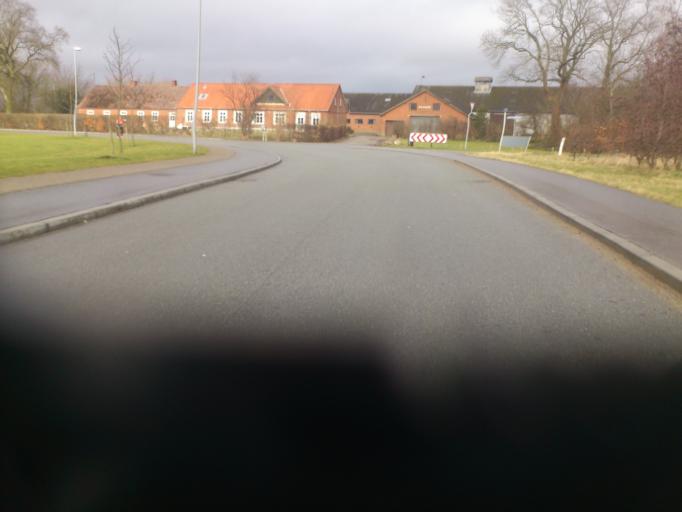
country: DK
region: South Denmark
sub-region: Fredericia Kommune
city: Fredericia
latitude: 55.5819
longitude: 9.7061
